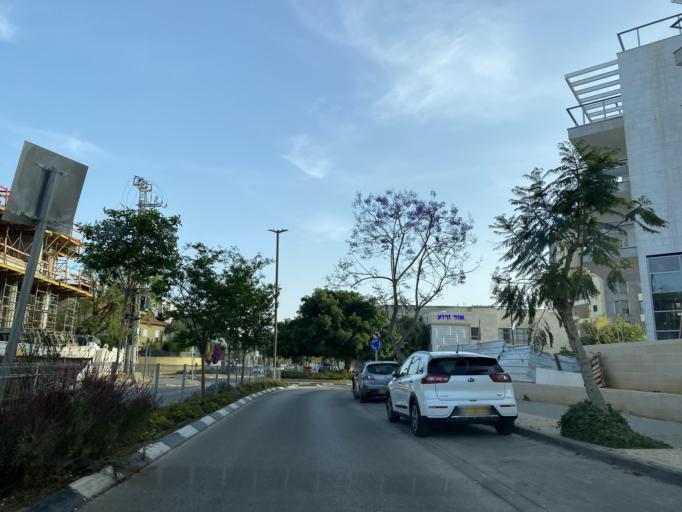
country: IL
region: Tel Aviv
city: Herzliyya
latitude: 32.1674
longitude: 34.8312
